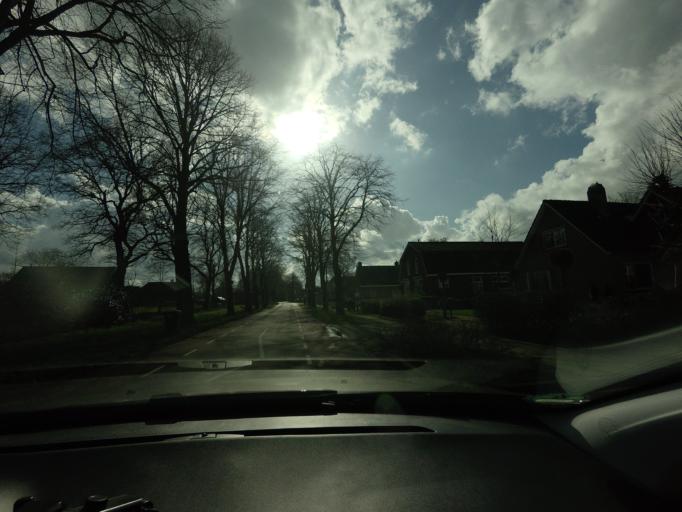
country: NL
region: Drenthe
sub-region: Gemeente Assen
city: Assen
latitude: 52.8742
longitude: 6.5878
